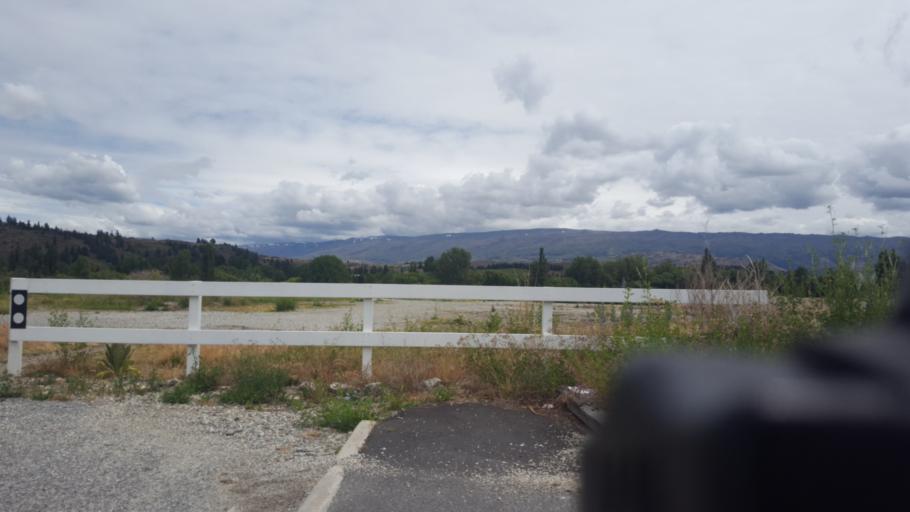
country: NZ
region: Otago
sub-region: Queenstown-Lakes District
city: Wanaka
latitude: -45.2506
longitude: 169.3789
